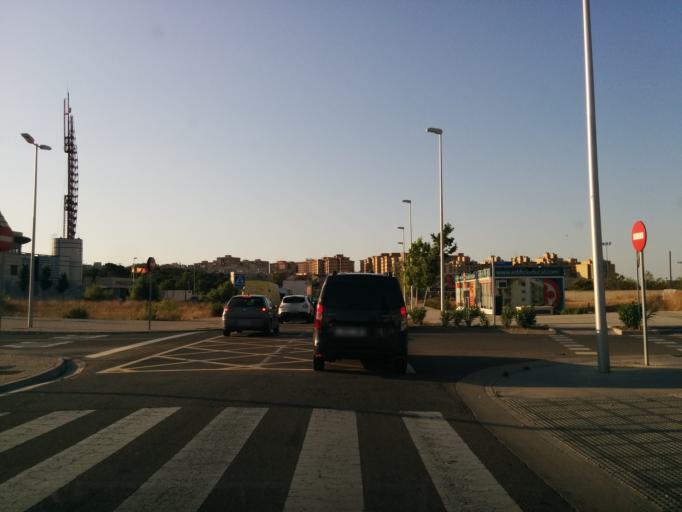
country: ES
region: Aragon
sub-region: Provincia de Zaragoza
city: Zaragoza
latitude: 41.6189
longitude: -0.8762
